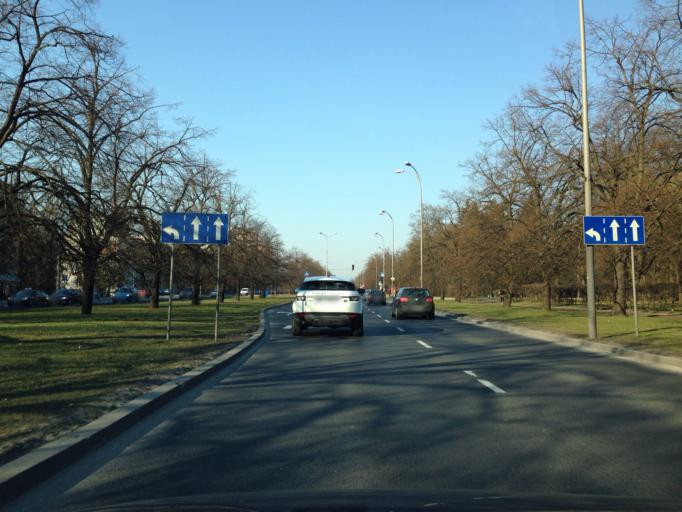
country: PL
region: Masovian Voivodeship
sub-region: Warszawa
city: Ochota
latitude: 52.2000
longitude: 20.9846
